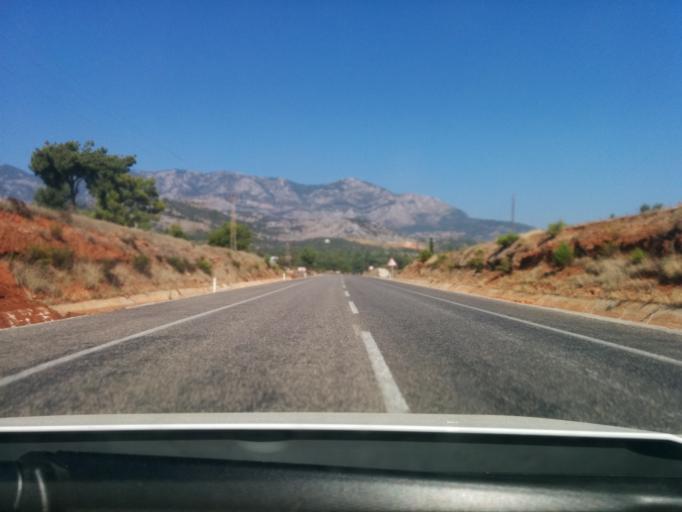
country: TR
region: Mugla
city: Esen
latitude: 36.4305
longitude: 29.2710
